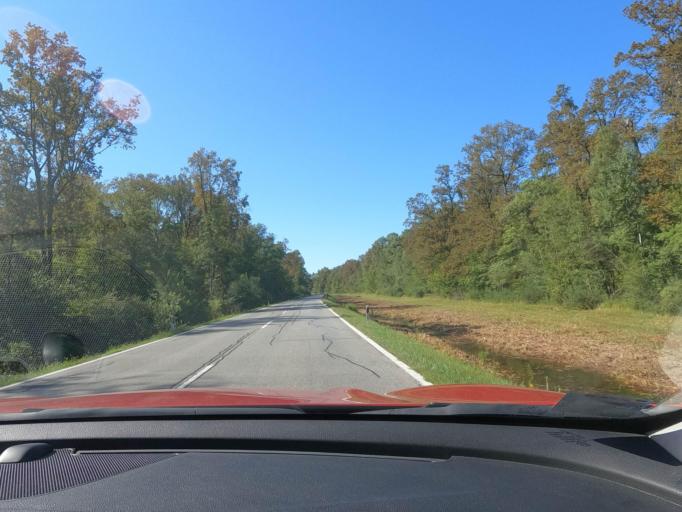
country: HR
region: Sisacko-Moslavacka
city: Budasevo
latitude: 45.4994
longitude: 16.5128
